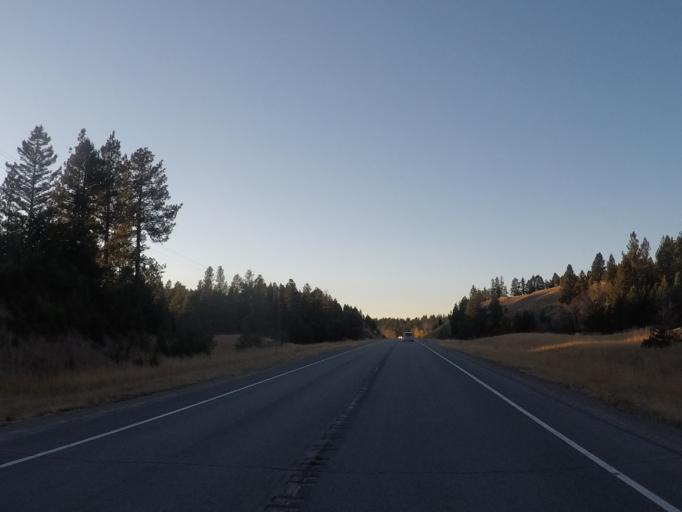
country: US
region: Montana
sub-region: Lewis and Clark County
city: Lincoln
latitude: 47.0115
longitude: -113.0635
